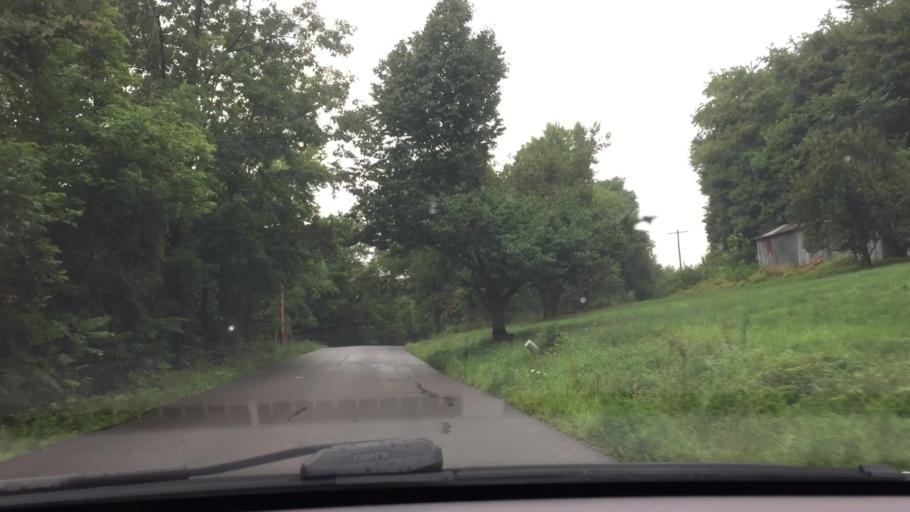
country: US
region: Pennsylvania
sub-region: Washington County
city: Muse
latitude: 40.3009
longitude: -80.1936
